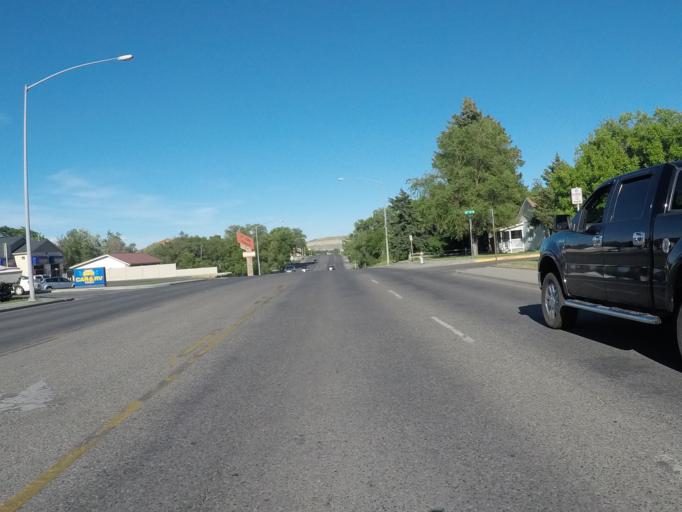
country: US
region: Montana
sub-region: Yellowstone County
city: Billings
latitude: 45.7770
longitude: -108.5492
